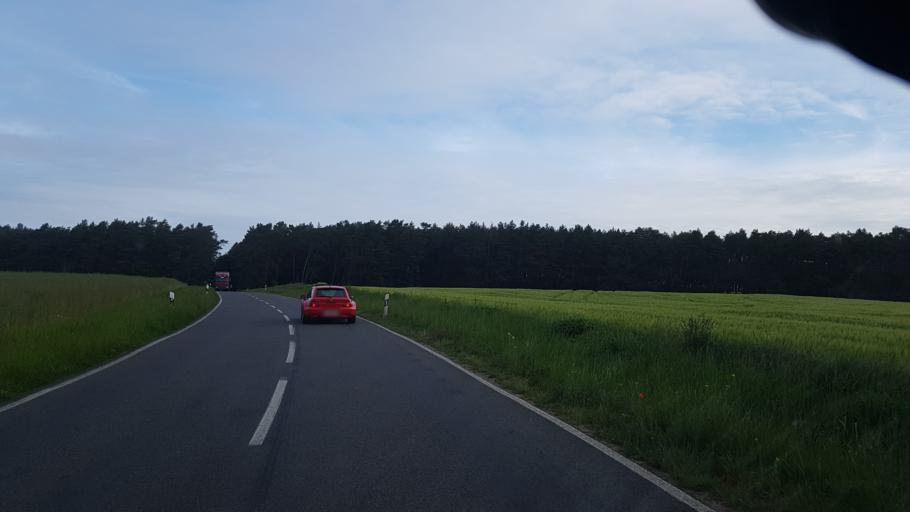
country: DE
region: Brandenburg
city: Baruth
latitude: 51.9906
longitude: 13.4824
